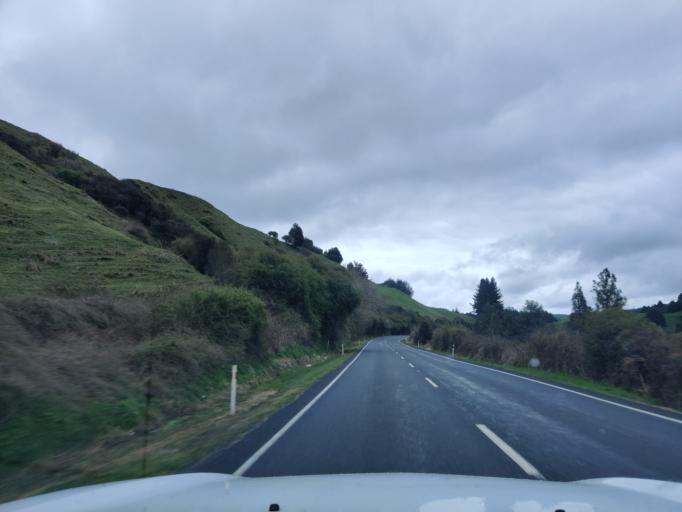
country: NZ
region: Waikato
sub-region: Otorohanga District
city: Otorohanga
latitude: -38.5924
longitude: 175.2190
